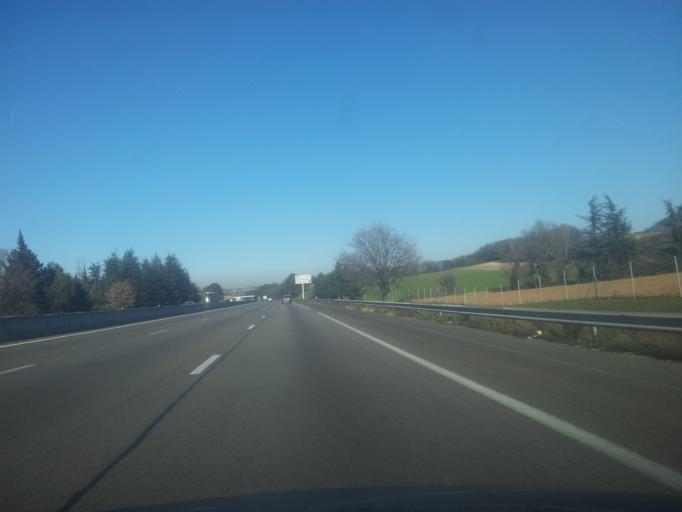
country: FR
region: Rhone-Alpes
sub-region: Departement de l'Ardeche
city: Cruas
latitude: 44.6555
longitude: 4.7954
